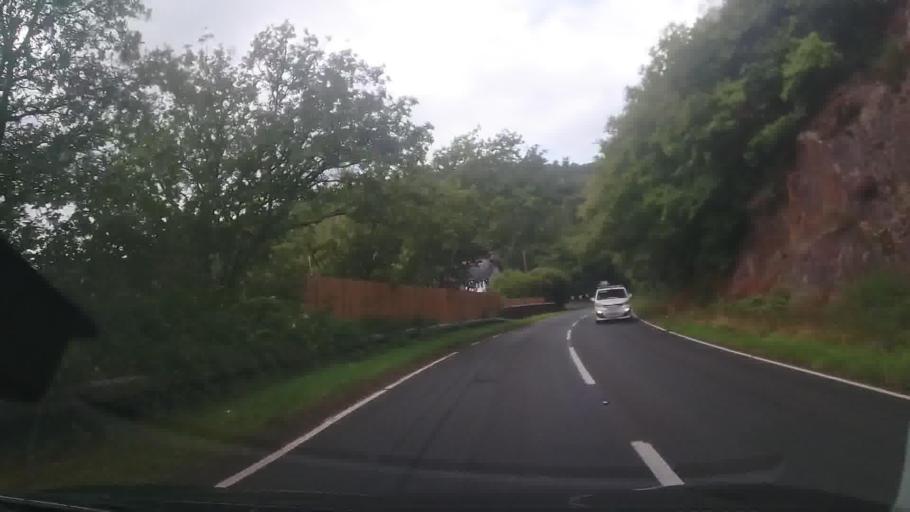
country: GB
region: Wales
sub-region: Gwynedd
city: Barmouth
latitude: 52.7354
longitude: -4.0203
